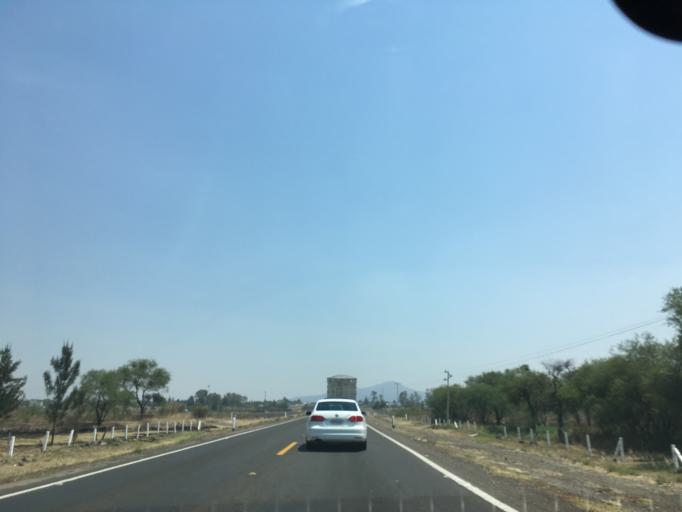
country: MX
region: Michoacan
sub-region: Cuitzeo
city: Cuamio
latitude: 20.0432
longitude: -101.1515
